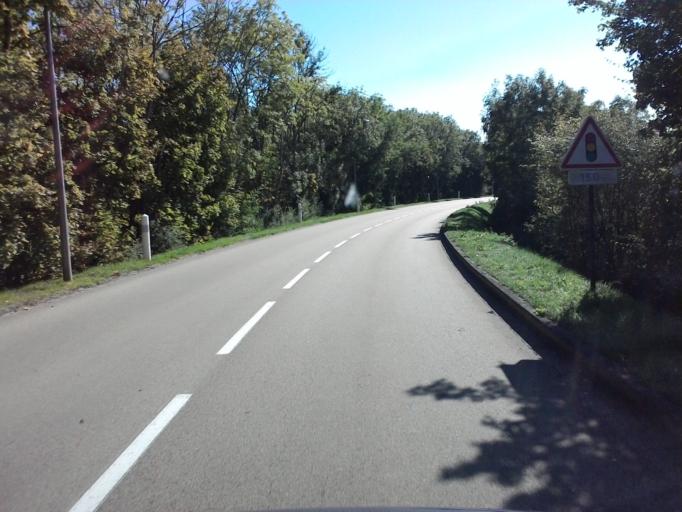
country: FR
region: Champagne-Ardenne
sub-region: Departement de la Haute-Marne
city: Chaumont
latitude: 48.1221
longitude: 5.1480
